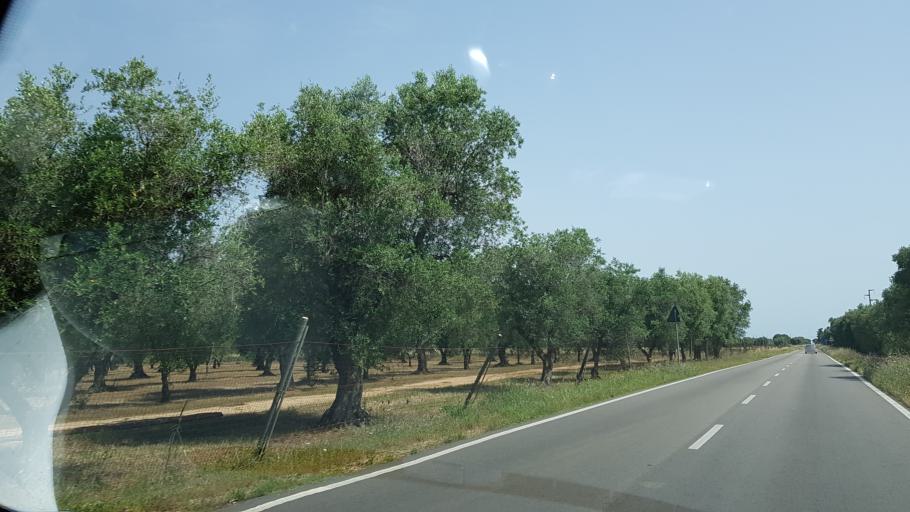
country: IT
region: Apulia
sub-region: Provincia di Brindisi
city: San Pancrazio Salentino
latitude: 40.3587
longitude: 17.8432
